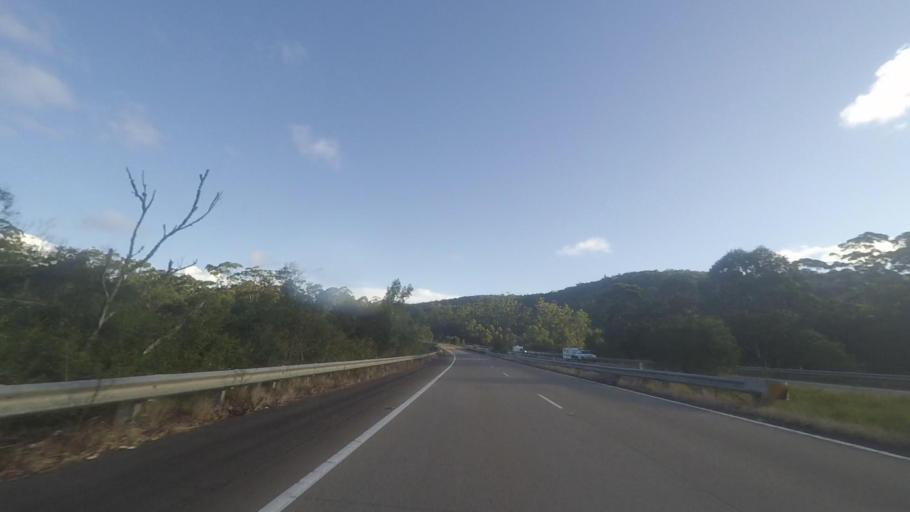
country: AU
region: New South Wales
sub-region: Great Lakes
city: Bulahdelah
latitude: -32.2723
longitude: 152.3286
